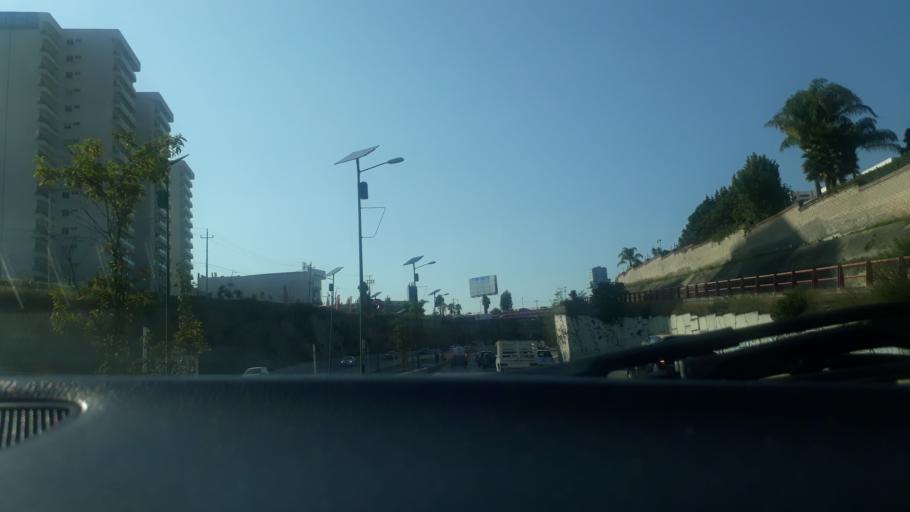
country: MX
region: Puebla
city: Tlazcalancingo
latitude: 18.9987
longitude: -98.2588
